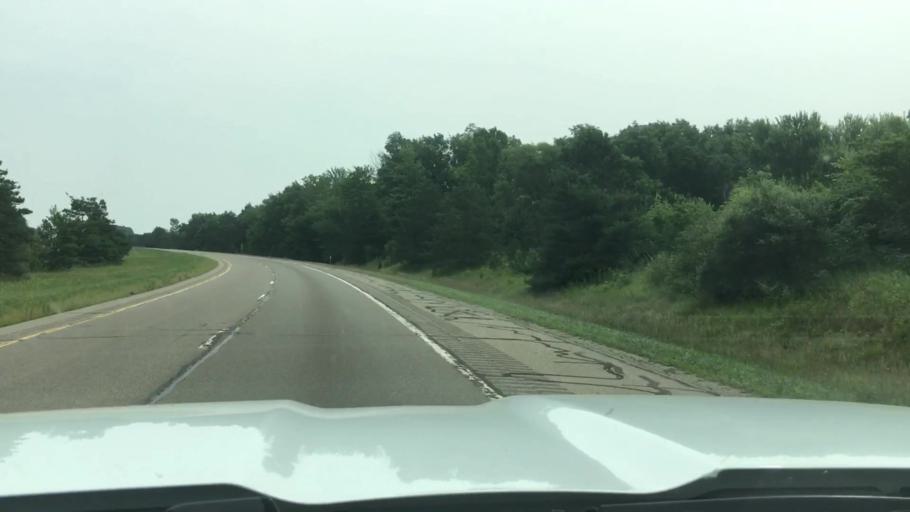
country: US
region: Michigan
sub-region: Eaton County
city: Dimondale
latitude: 42.6659
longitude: -84.6388
